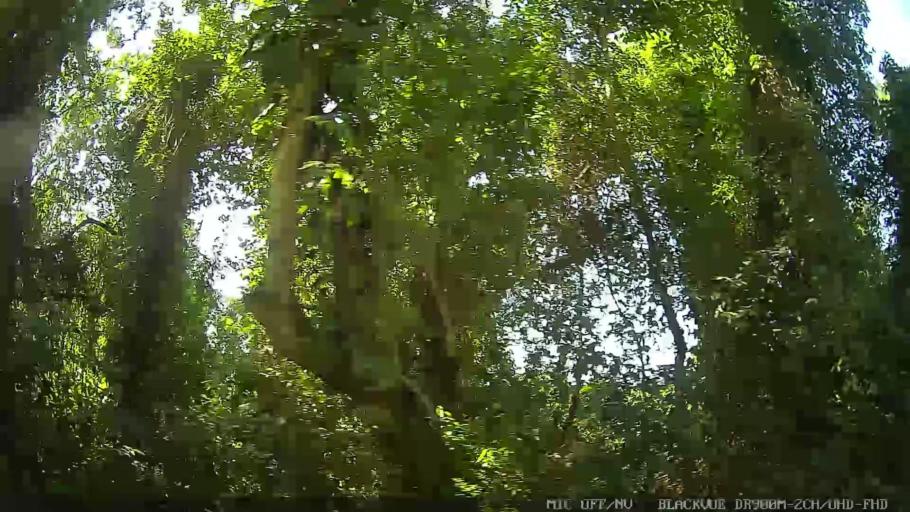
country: BR
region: Sao Paulo
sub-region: Santos
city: Santos
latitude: -24.0002
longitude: -46.3119
